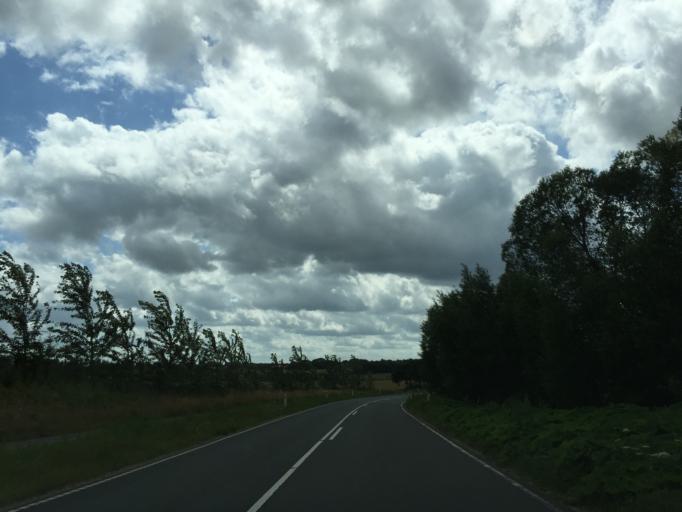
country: DK
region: Central Jutland
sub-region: Silkeborg Kommune
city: Svejbaek
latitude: 56.1976
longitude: 9.7059
